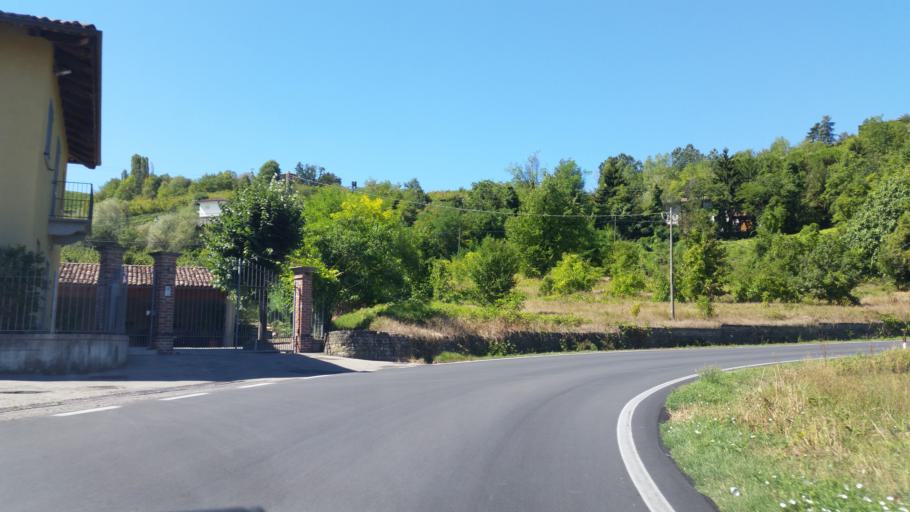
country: IT
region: Piedmont
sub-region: Provincia di Cuneo
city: Alba
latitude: 44.6924
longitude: 8.0526
